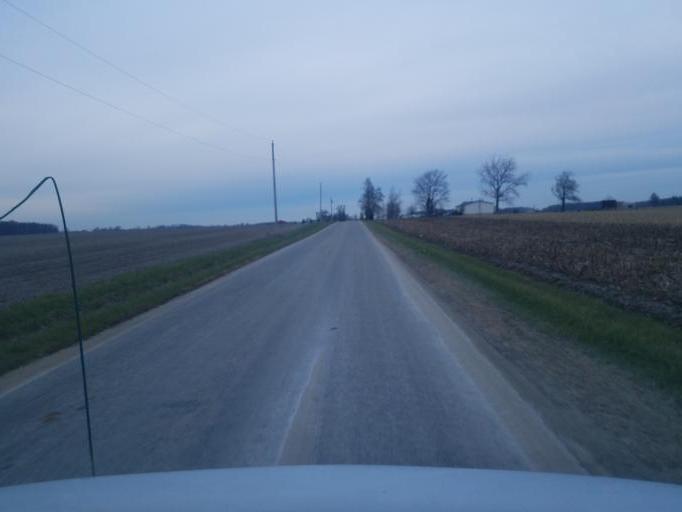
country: US
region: Indiana
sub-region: Adams County
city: Decatur
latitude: 40.7464
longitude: -84.8796
